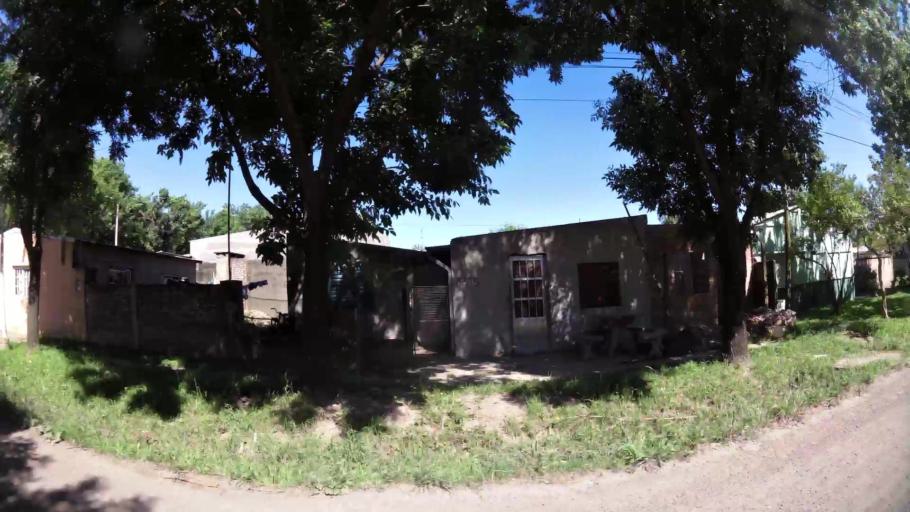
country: AR
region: Santa Fe
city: Esperanza
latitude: -31.4532
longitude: -60.9424
